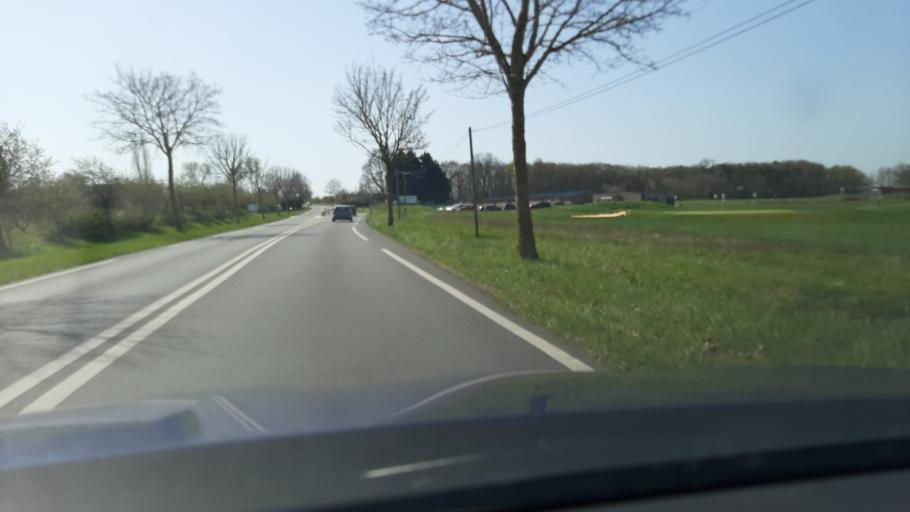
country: FR
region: Pays de la Loire
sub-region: Departement de Maine-et-Loire
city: Pellouailles-les-Vignes
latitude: 47.5102
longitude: -0.4784
